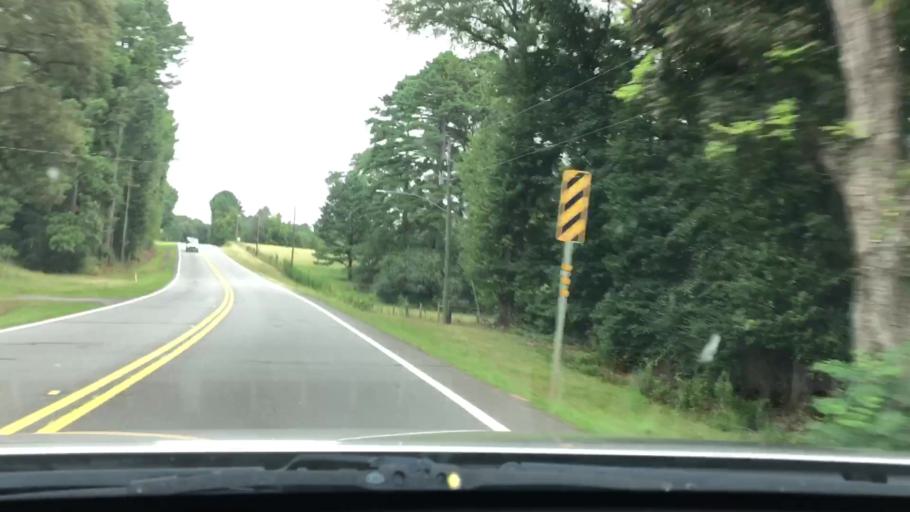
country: US
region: Georgia
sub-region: Upson County
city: Hannahs Mill
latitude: 33.0174
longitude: -84.4976
